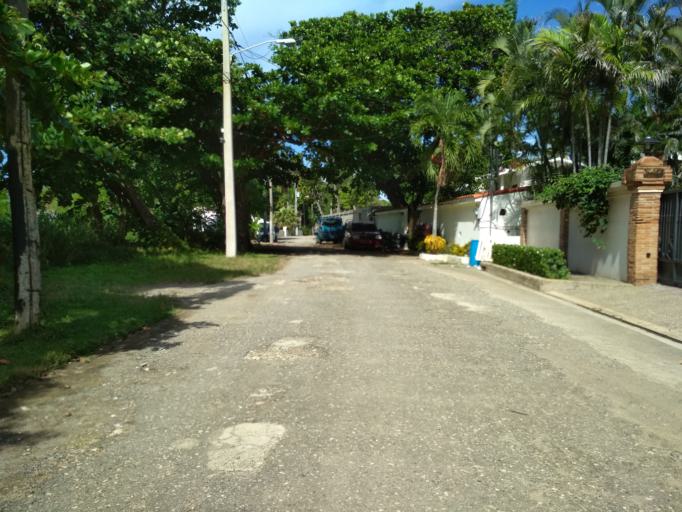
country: DO
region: Puerto Plata
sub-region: Puerto Plata
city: Puerto Plata
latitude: 19.8086
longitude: -70.7065
